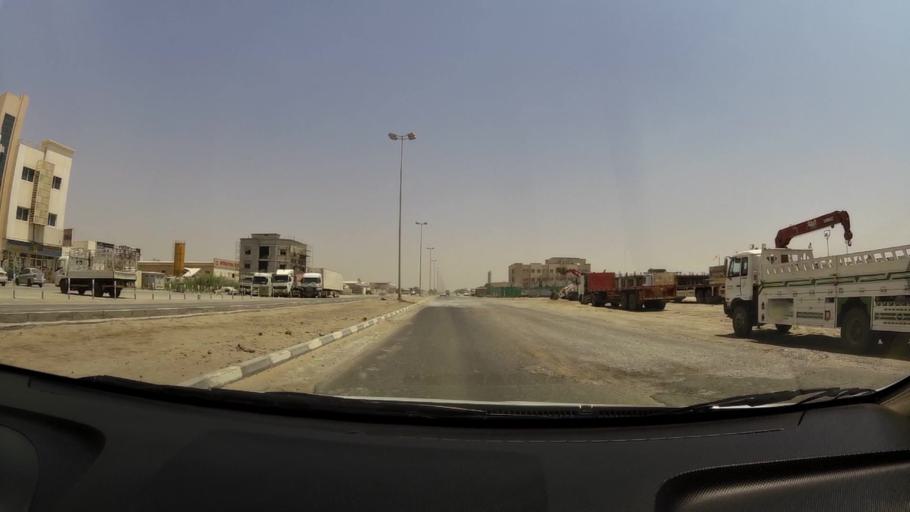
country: AE
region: Umm al Qaywayn
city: Umm al Qaywayn
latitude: 25.5108
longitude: 55.5581
